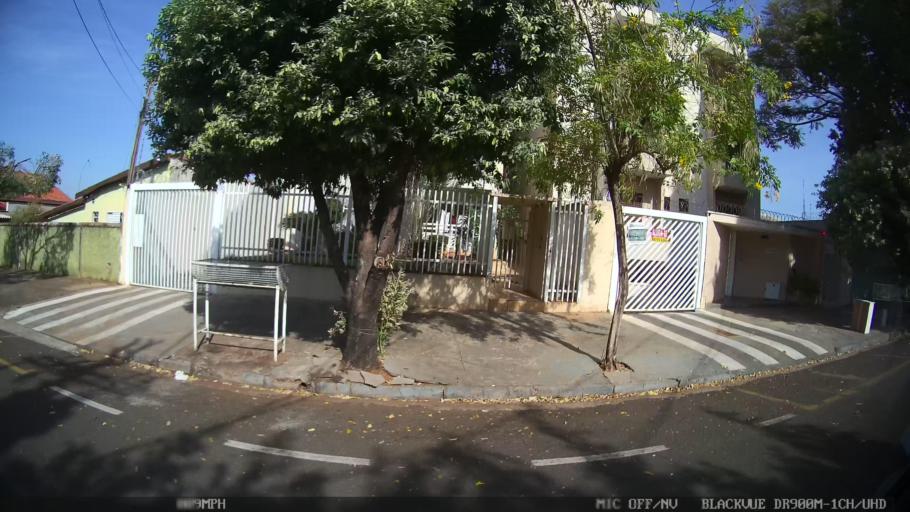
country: BR
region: Sao Paulo
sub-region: Sao Jose Do Rio Preto
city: Sao Jose do Rio Preto
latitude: -20.7989
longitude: -49.4152
